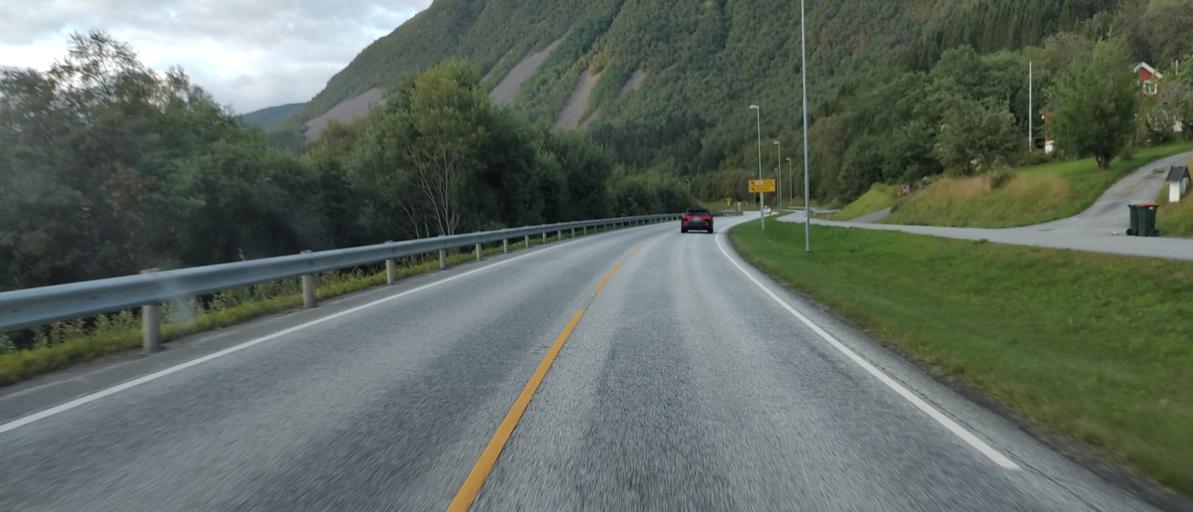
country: NO
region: More og Romsdal
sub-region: Molde
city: Molde
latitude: 62.8004
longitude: 7.2413
